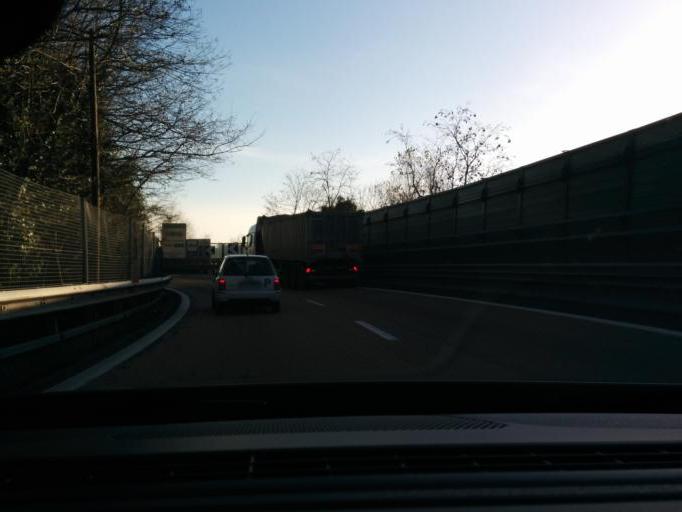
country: IT
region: Liguria
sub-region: Provincia di Genova
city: Genoa
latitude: 44.4409
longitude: 8.8930
